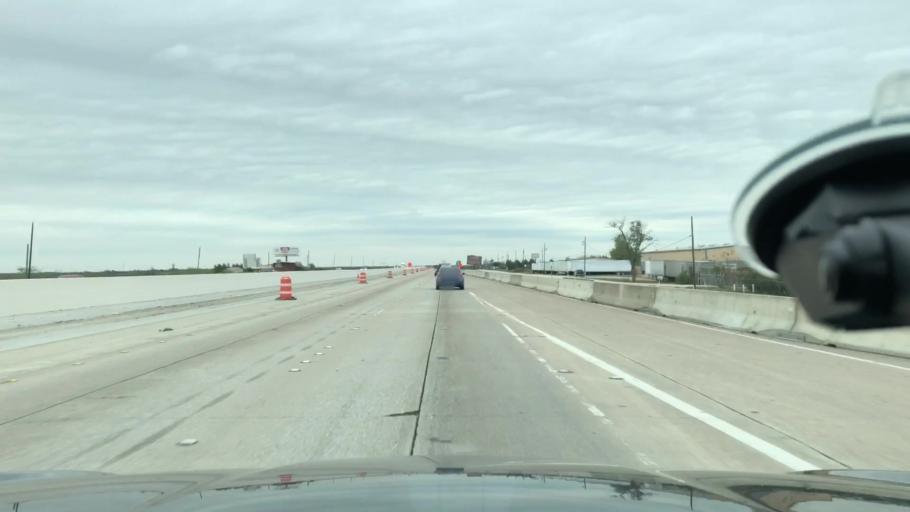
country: US
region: Texas
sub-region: Ellis County
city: Oak Leaf
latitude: 32.4784
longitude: -96.8337
